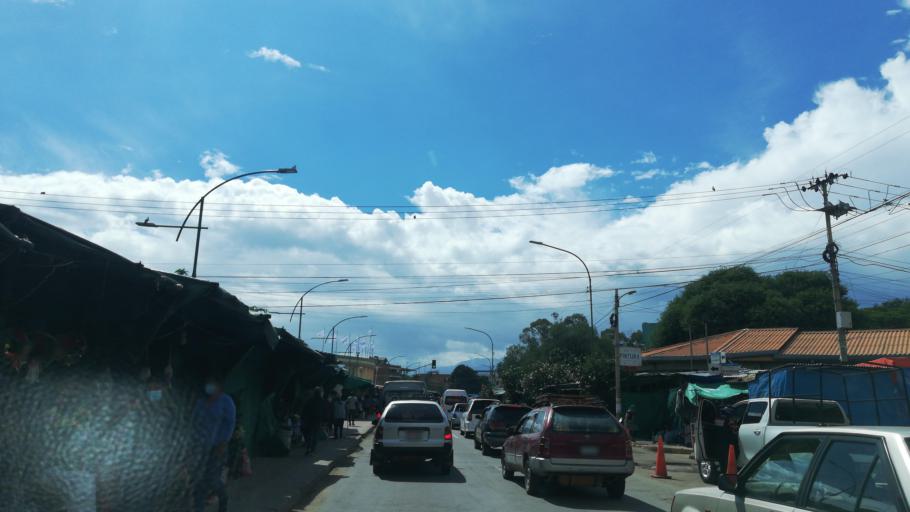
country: BO
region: Cochabamba
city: Cochabamba
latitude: -17.4172
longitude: -66.1581
